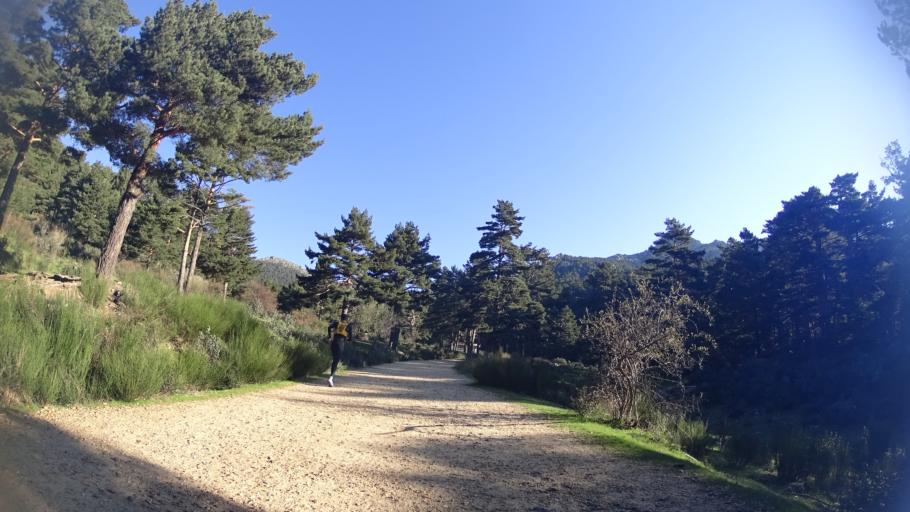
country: ES
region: Madrid
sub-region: Provincia de Madrid
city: Navacerrada
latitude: 40.7573
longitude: -3.9933
